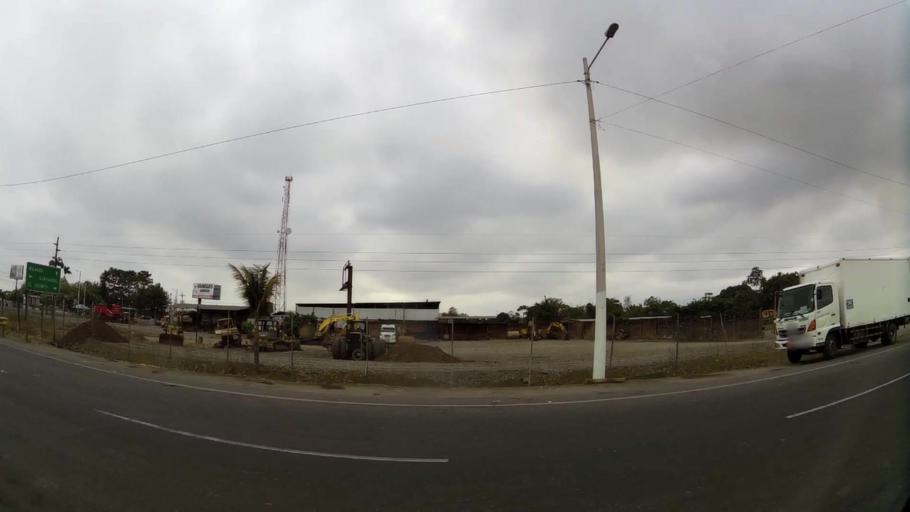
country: EC
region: Guayas
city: Yaguachi Nuevo
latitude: -2.2529
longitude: -79.6358
